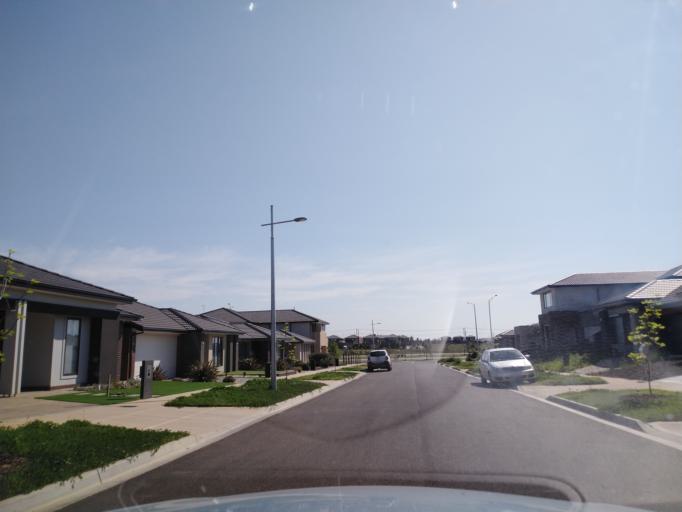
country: AU
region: Victoria
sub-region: Wyndham
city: Williams Landing
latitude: -37.8402
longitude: 144.7330
